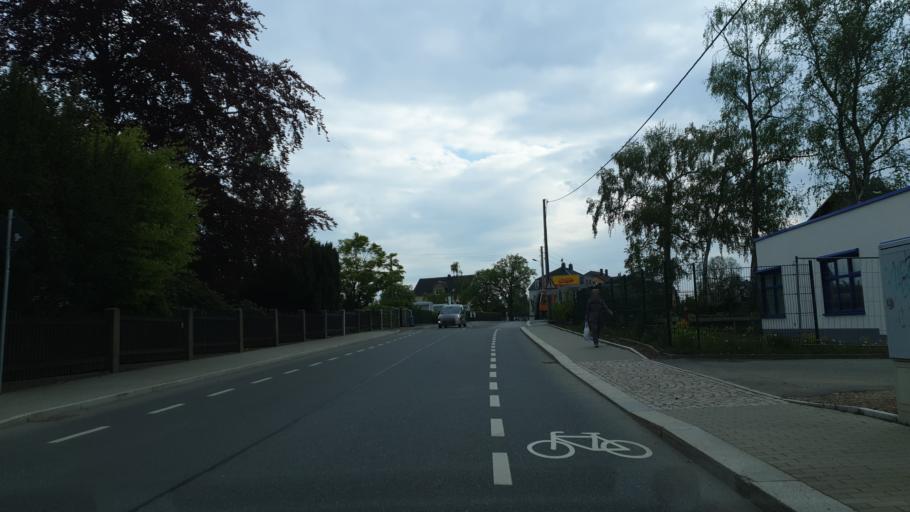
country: DE
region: Saxony
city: Lugau
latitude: 50.7350
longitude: 12.7442
